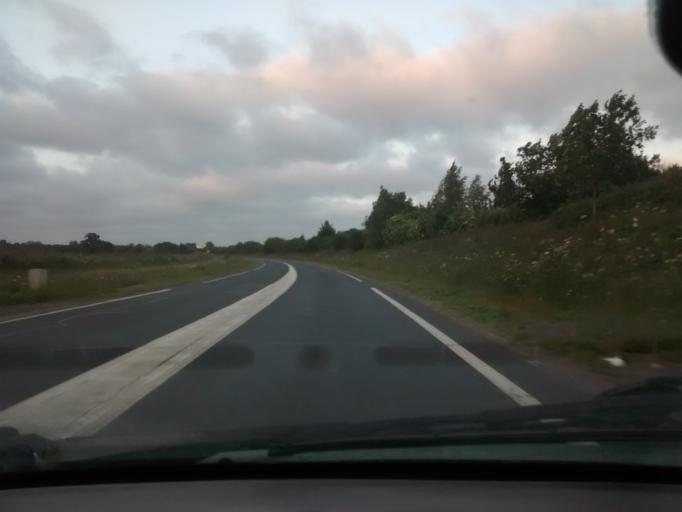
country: FR
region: Lower Normandy
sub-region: Departement de la Manche
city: Agneaux
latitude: 49.0984
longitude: -1.1084
